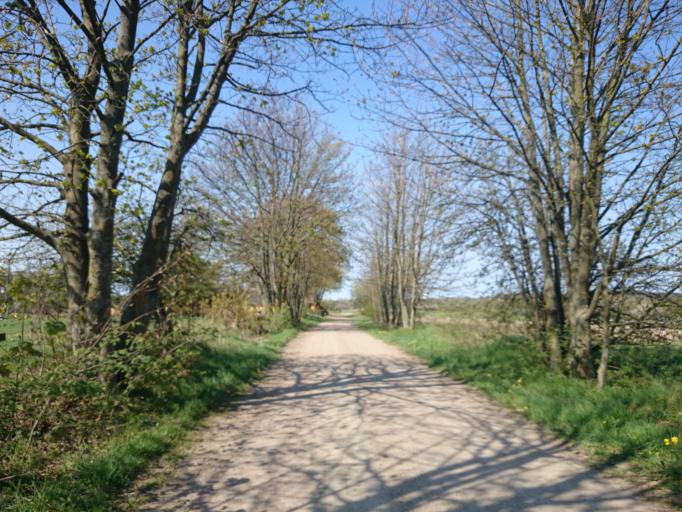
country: SE
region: Skane
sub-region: Lunds Kommun
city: Genarp
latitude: 55.6678
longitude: 13.3917
